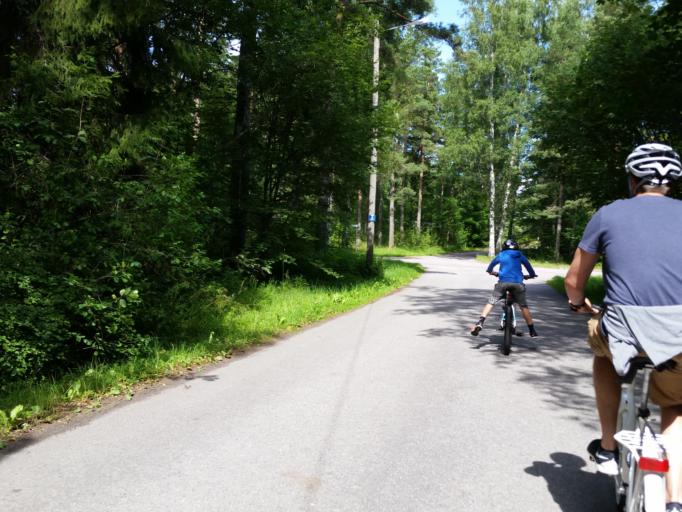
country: FI
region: Uusimaa
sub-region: Raaseporin
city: Hanko
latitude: 59.8304
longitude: 22.9298
